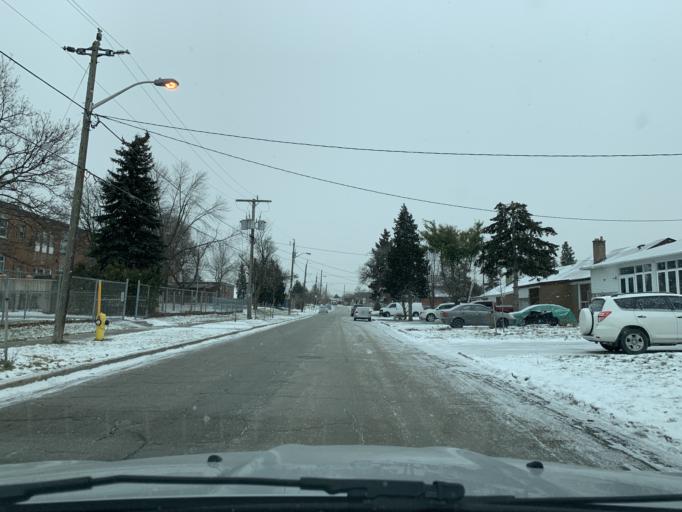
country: CA
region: Ontario
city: Concord
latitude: 43.7361
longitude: -79.4868
